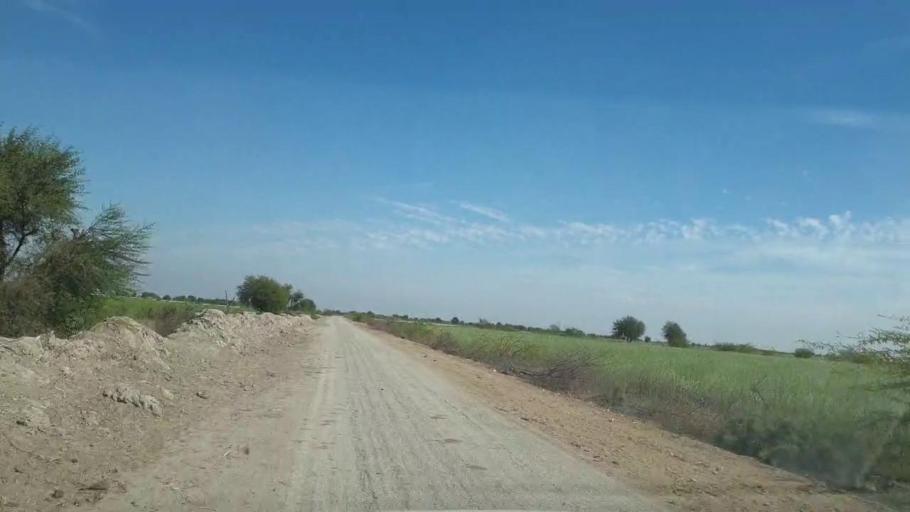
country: PK
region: Sindh
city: Pithoro
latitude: 25.5774
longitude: 69.3007
